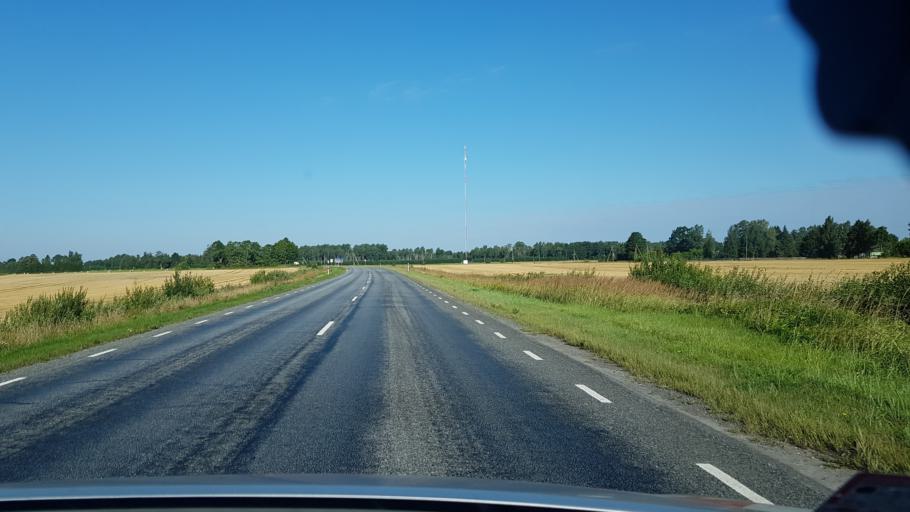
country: EE
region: Laeaene
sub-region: Lihula vald
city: Lihula
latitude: 58.5288
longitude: 24.0607
